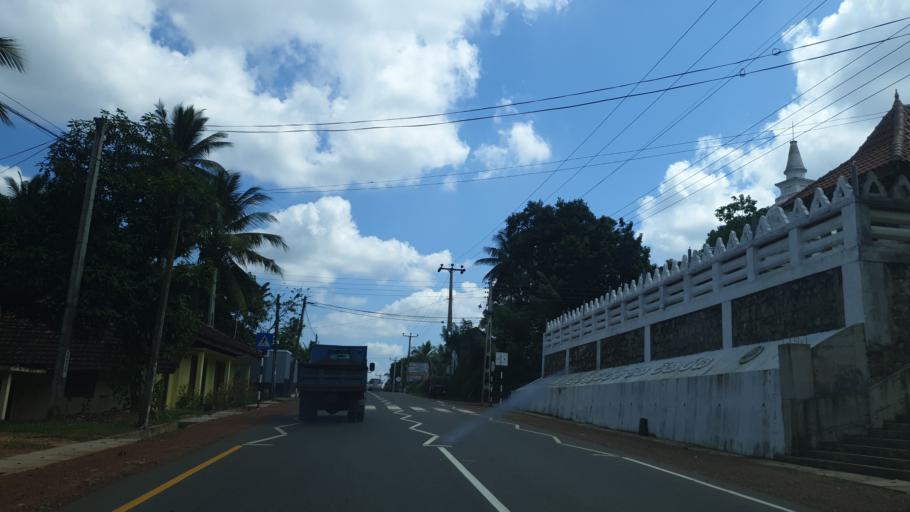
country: LK
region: Western
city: Panadura
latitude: 6.6658
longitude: 79.9642
